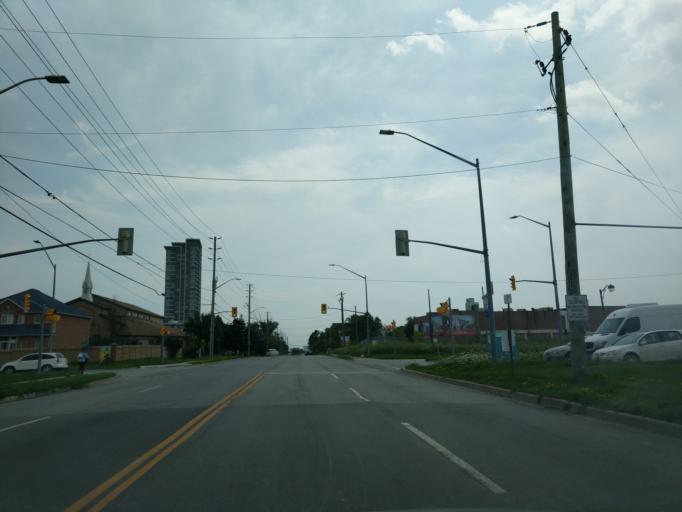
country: CA
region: Ontario
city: Markham
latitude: 43.8299
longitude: -79.3014
